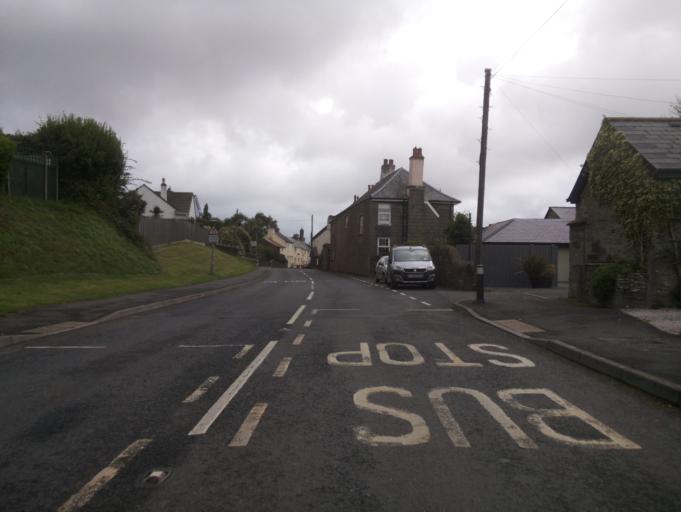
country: GB
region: England
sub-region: Devon
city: Salcombe
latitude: 50.2729
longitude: -3.6982
